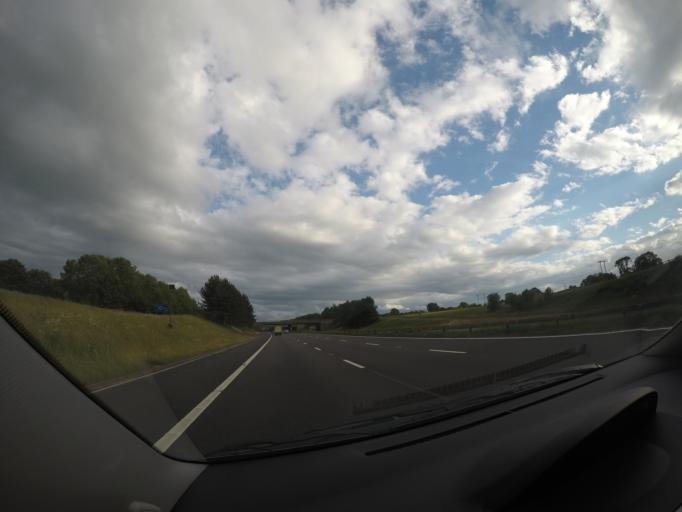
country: GB
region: England
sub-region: Cumbria
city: Penrith
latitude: 54.6958
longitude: -2.7913
